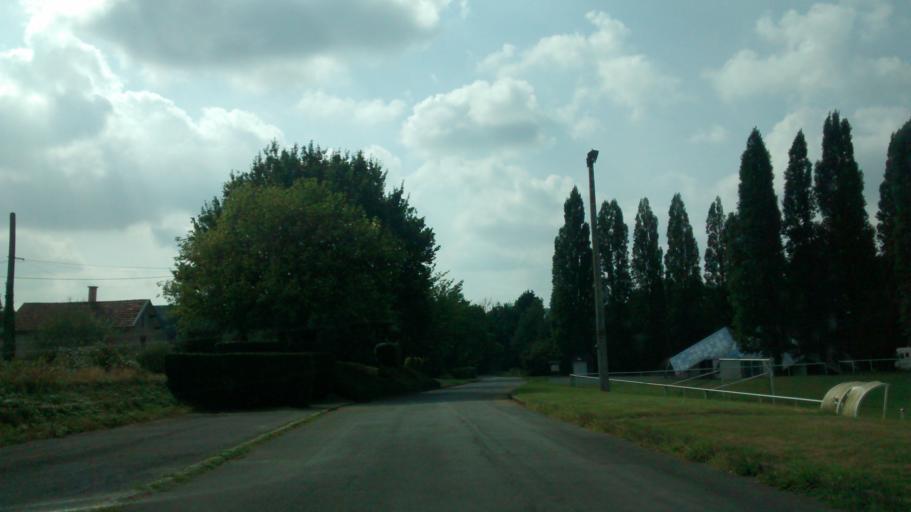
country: FR
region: Brittany
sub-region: Departement d'Ille-et-Vilaine
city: Chatillon-en-Vendelais
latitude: 48.2304
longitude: -1.1795
